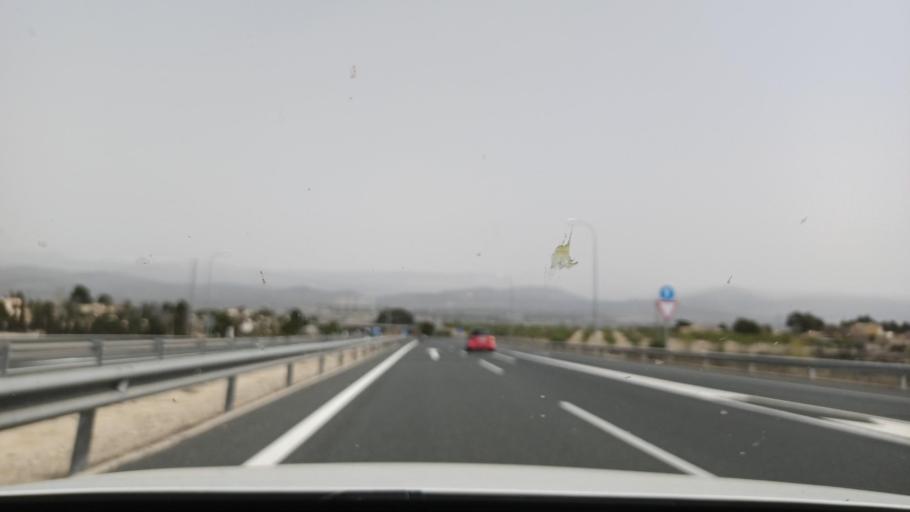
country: ES
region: Valencia
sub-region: Provincia de Alicante
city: Castalla
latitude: 38.5777
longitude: -0.6519
